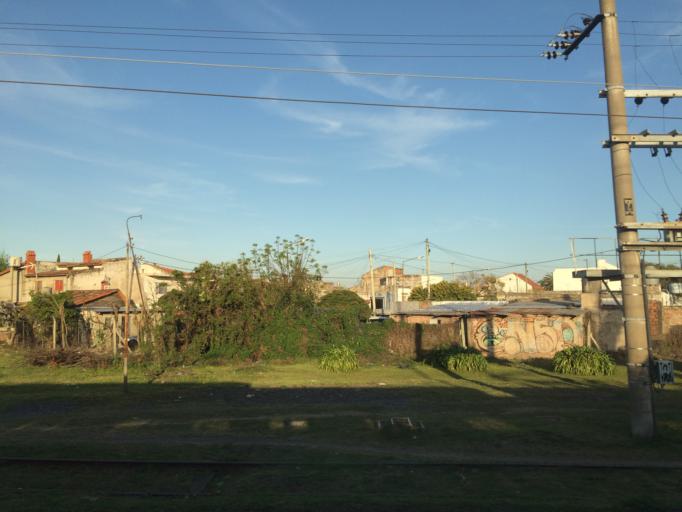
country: AR
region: Buenos Aires
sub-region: Partido de Lanus
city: Lanus
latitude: -34.6934
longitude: -58.3854
